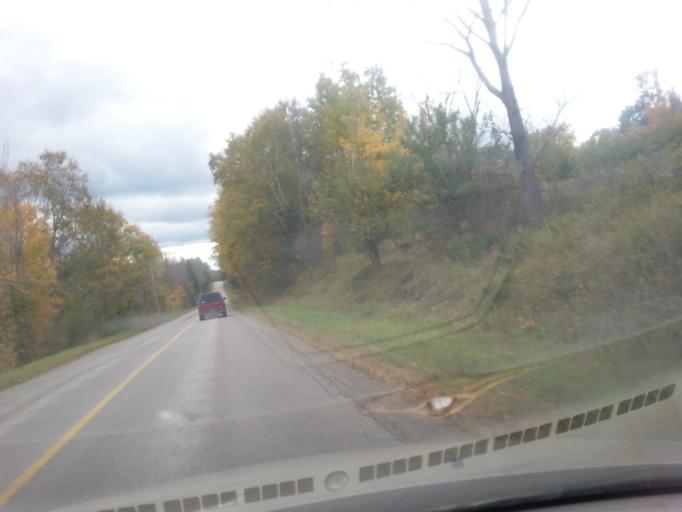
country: CA
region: Ontario
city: Pembroke
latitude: 45.5107
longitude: -77.0269
